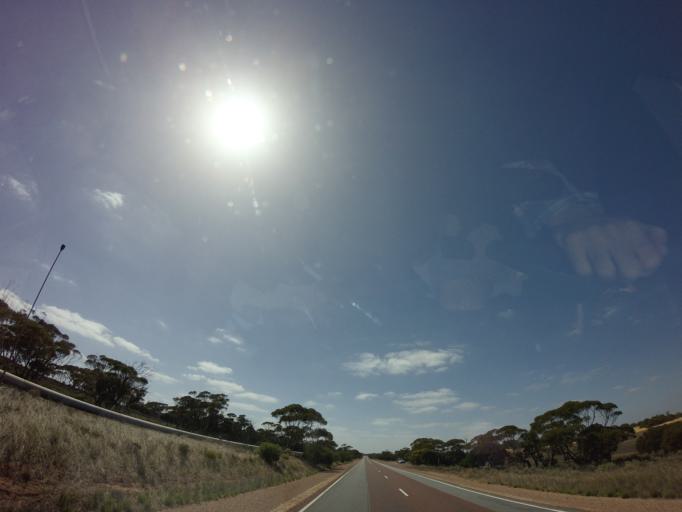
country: AU
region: South Australia
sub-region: Kimba
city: Caralue
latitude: -33.0836
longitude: 135.5001
